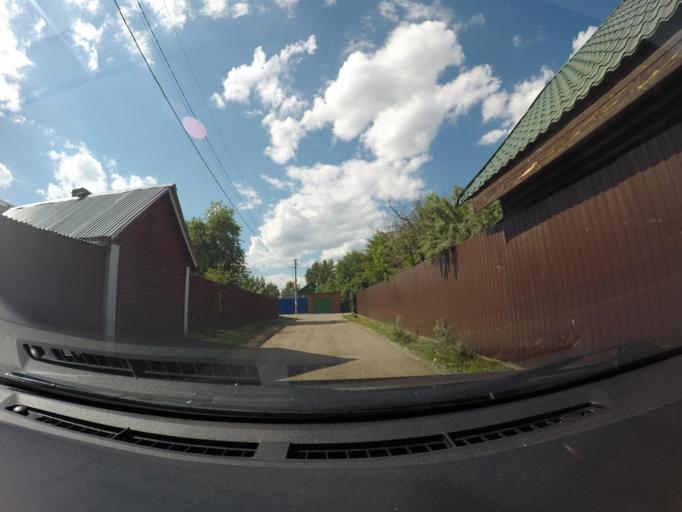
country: RU
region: Moskovskaya
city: Rechitsy
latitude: 55.5787
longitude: 38.5059
